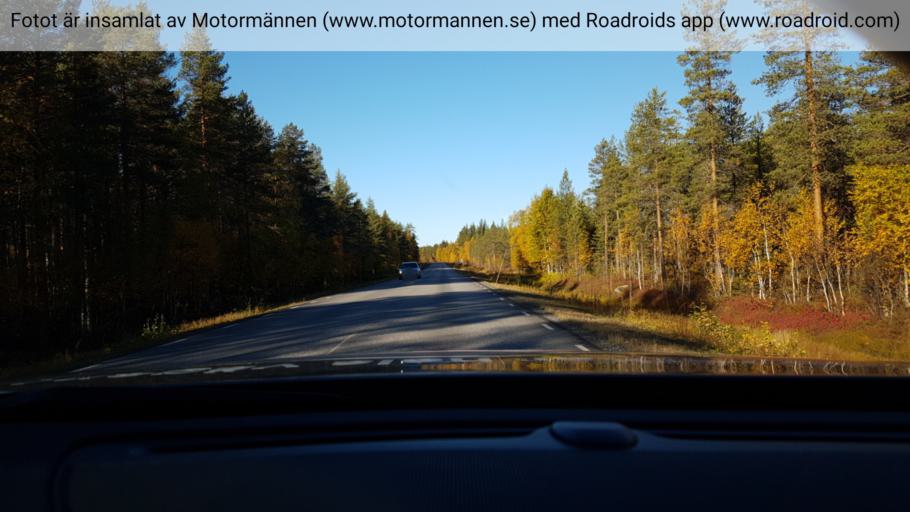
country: SE
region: Norrbotten
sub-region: Pitea Kommun
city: Roknas
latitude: 65.3420
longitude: 20.9621
